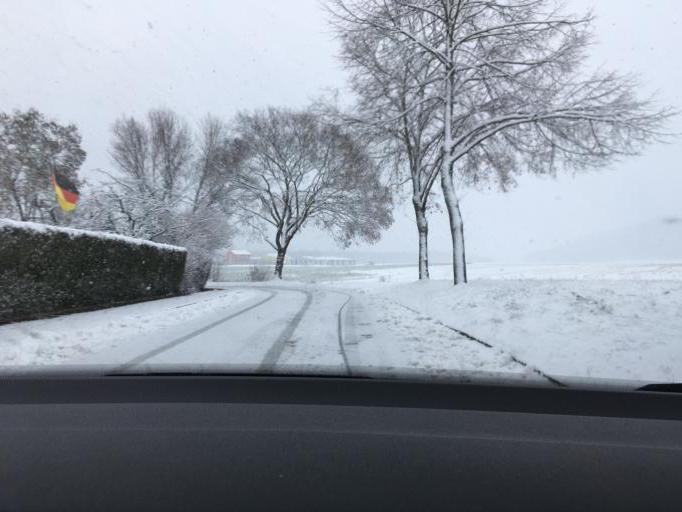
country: DE
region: Baden-Wuerttemberg
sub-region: Freiburg Region
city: Gottmadingen
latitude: 47.7315
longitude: 8.7912
